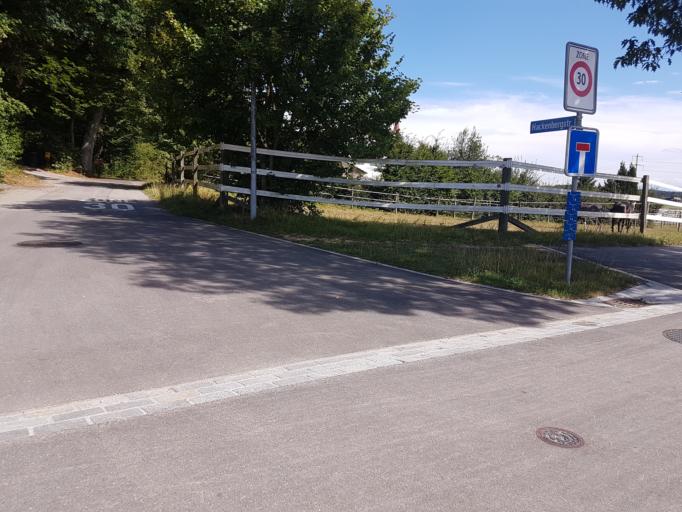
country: CH
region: Zurich
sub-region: Bezirk Pfaeffikon
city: Effretikon
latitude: 47.4203
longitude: 8.6850
